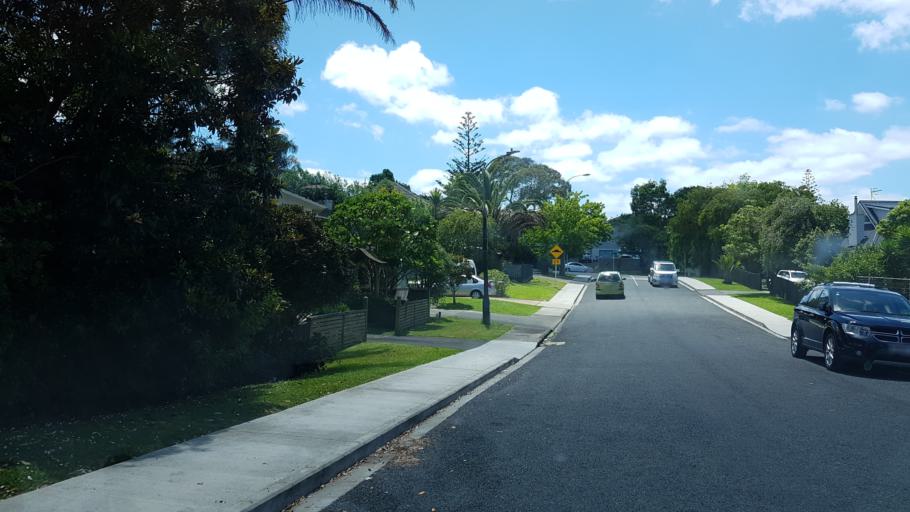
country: NZ
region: Auckland
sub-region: Auckland
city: North Shore
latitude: -36.7829
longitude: 174.7292
